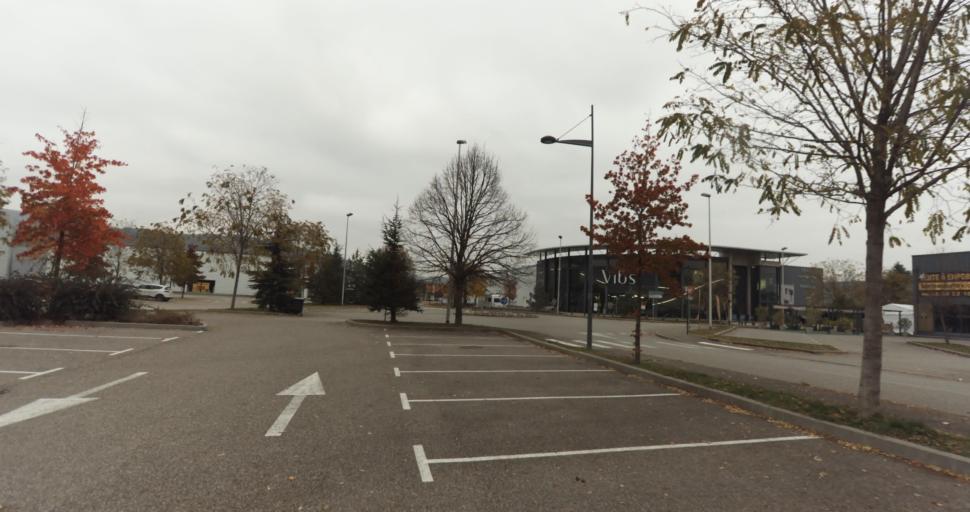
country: FR
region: Rhone-Alpes
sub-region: Departement de la Haute-Savoie
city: Epagny
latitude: 45.9341
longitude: 6.0815
